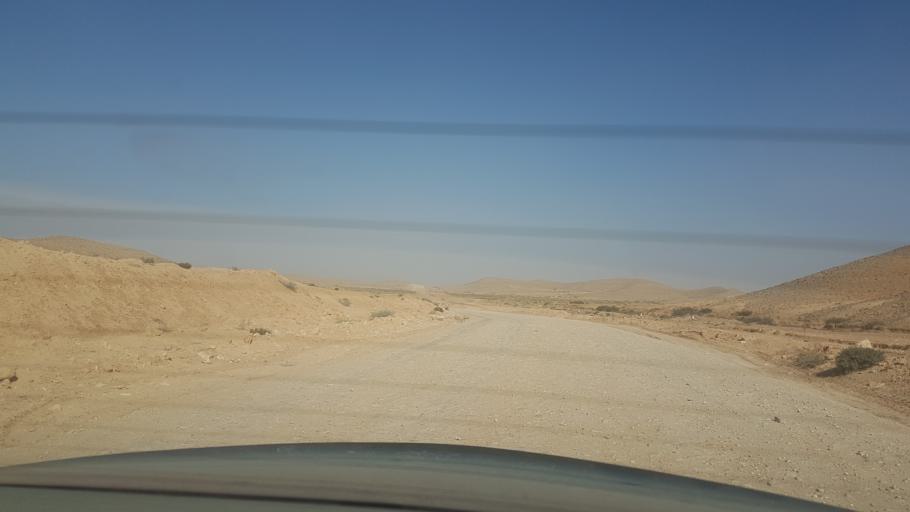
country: TN
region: Qabis
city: Matmata
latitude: 33.6400
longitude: 9.7366
